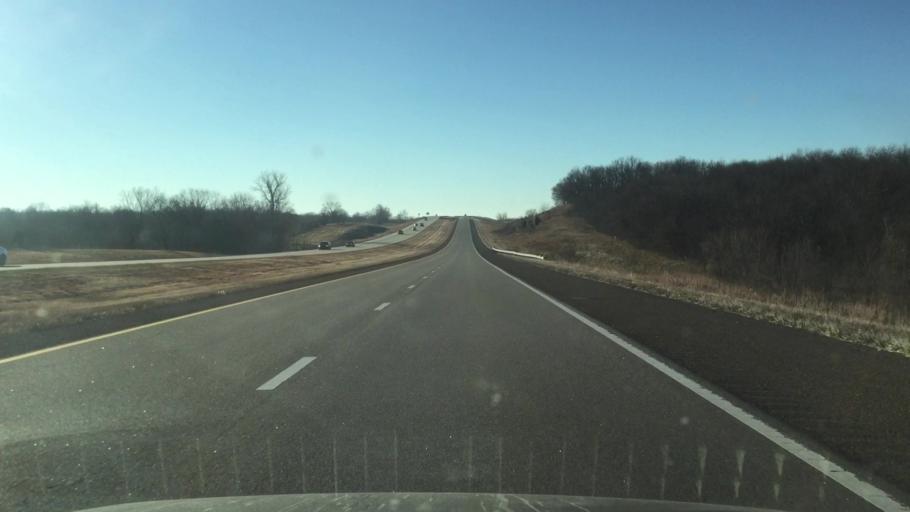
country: US
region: Kansas
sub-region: Miami County
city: Paola
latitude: 38.6426
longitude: -94.8359
